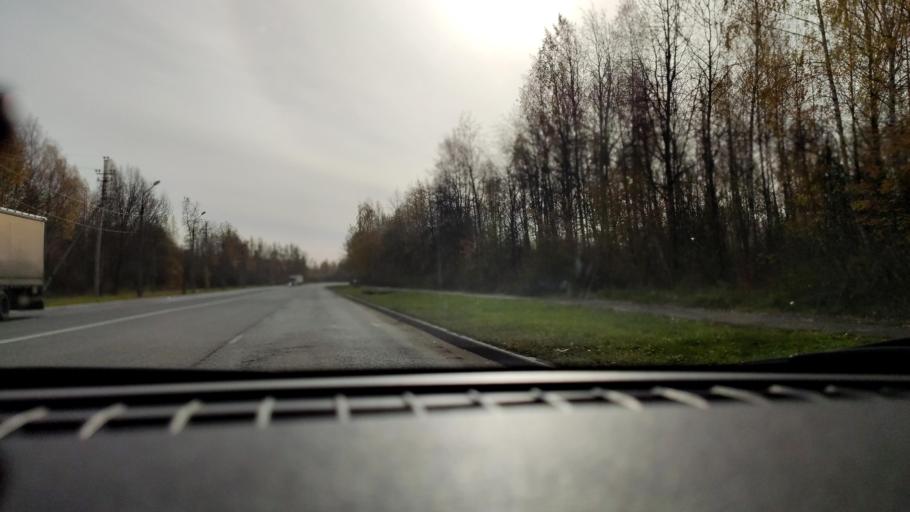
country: RU
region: Perm
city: Polazna
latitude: 58.1320
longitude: 56.4042
